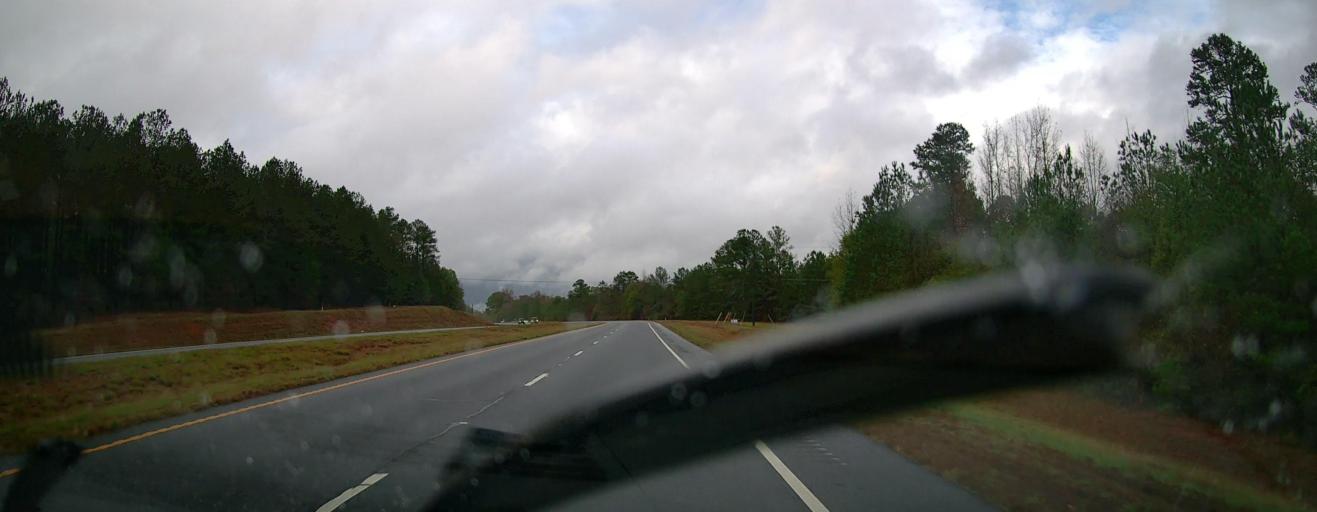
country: US
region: Georgia
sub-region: Jackson County
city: Nicholson
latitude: 34.0738
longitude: -83.4241
